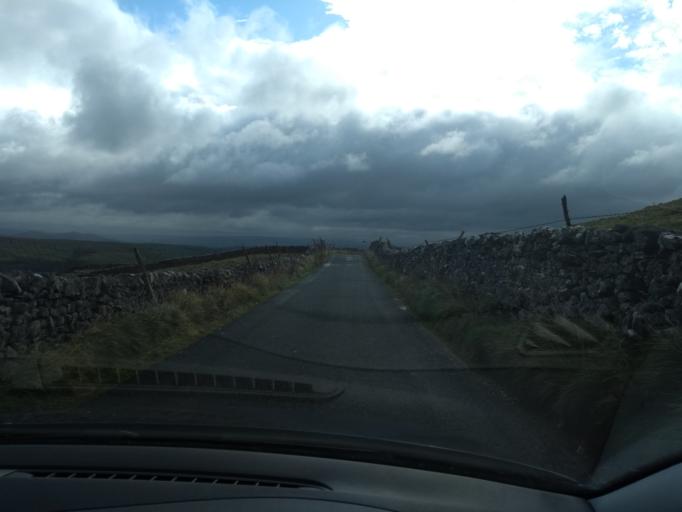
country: GB
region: England
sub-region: North Yorkshire
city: Settle
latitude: 54.0744
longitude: -2.1671
